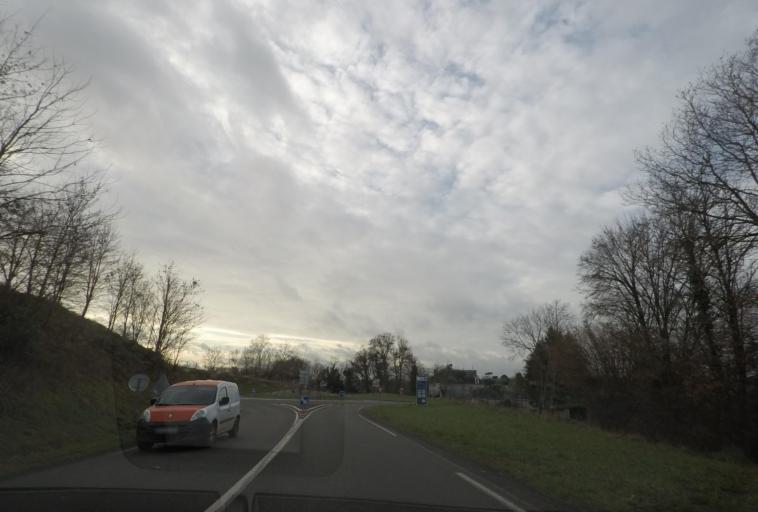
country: FR
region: Pays de la Loire
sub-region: Departement de la Sarthe
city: Saint-Calais
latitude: 47.9377
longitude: 0.7479
